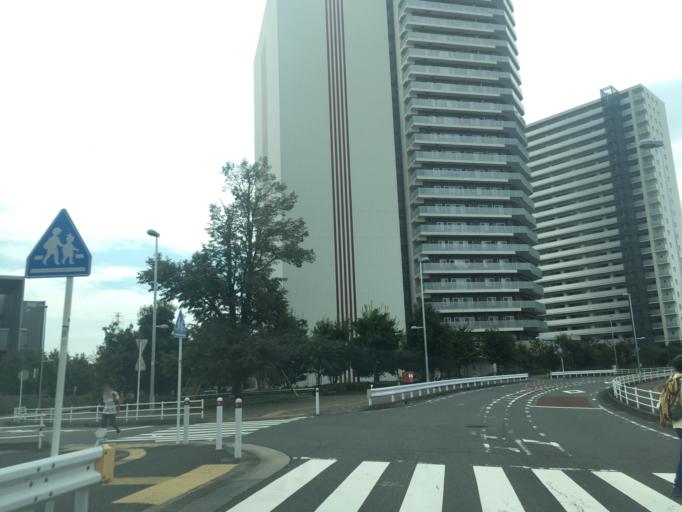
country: JP
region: Tokyo
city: Hachioji
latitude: 35.5908
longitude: 139.3519
